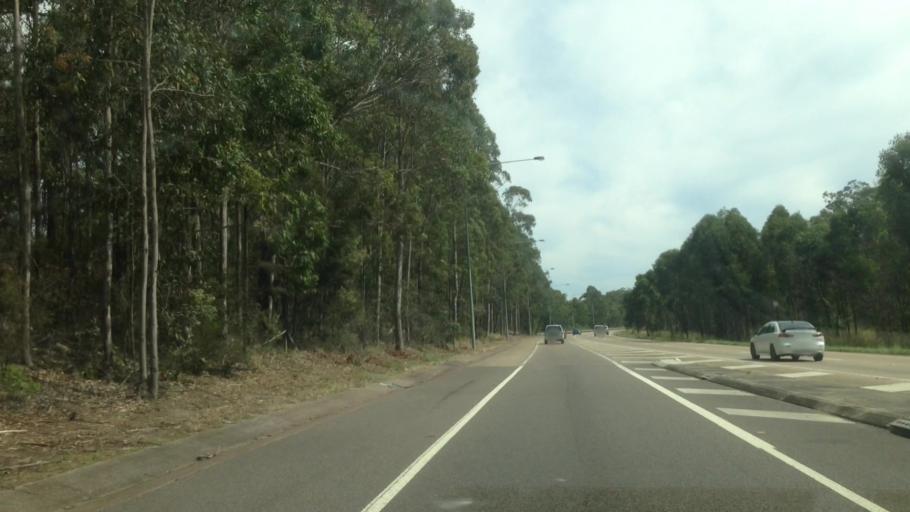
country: AU
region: New South Wales
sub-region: Lake Macquarie Shire
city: Holmesville
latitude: -32.8925
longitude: 151.5973
